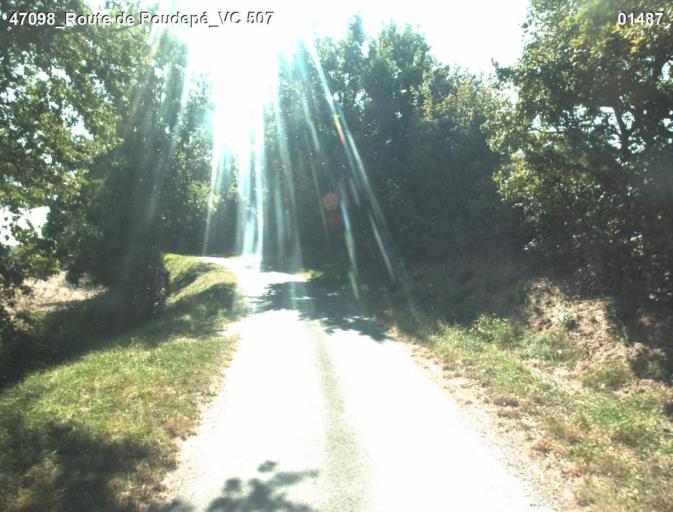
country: FR
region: Aquitaine
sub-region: Departement du Lot-et-Garonne
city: Nerac
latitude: 44.1065
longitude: 0.4036
